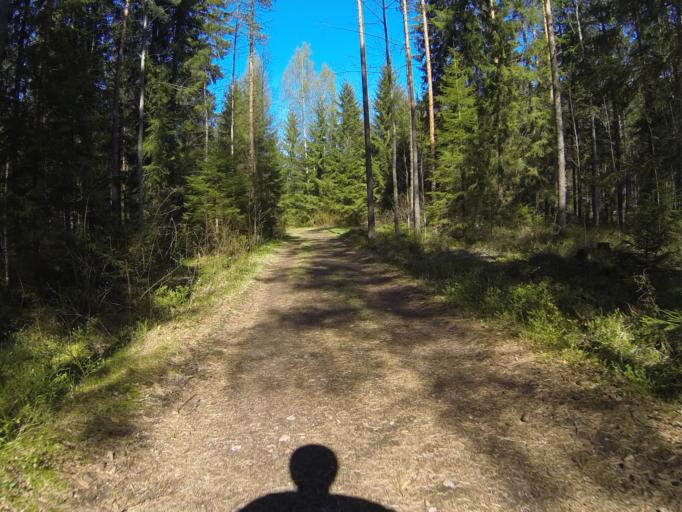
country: FI
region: Varsinais-Suomi
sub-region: Salo
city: Salo
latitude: 60.3990
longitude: 23.2019
